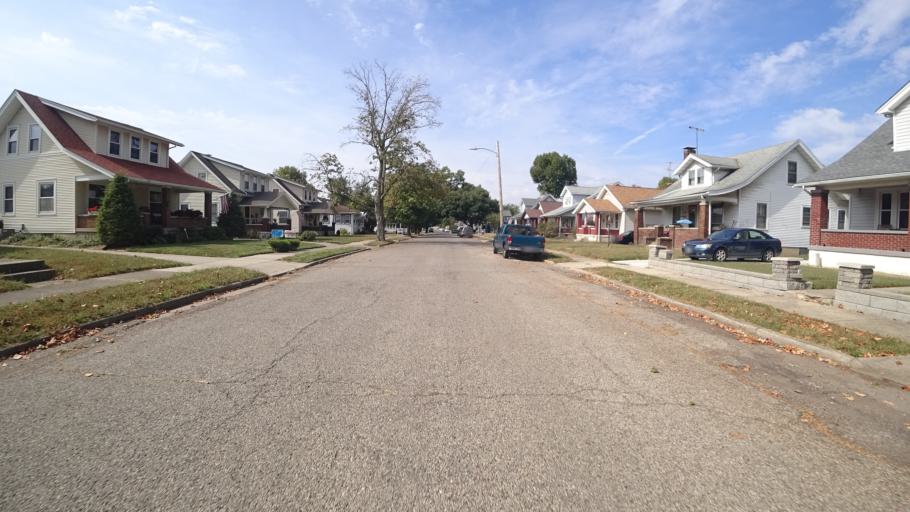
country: US
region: Ohio
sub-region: Butler County
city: Fairfield
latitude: 39.3627
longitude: -84.5519
